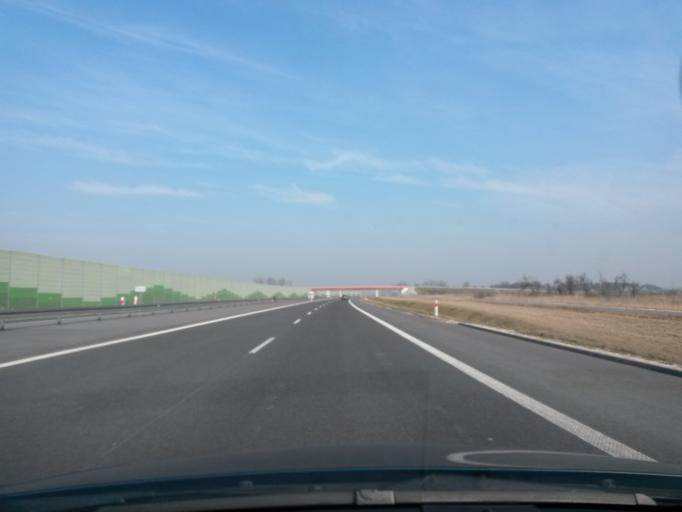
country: PL
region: Lodz Voivodeship
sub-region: Powiat kutnowski
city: Krzyzanow
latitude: 52.1440
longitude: 19.4824
